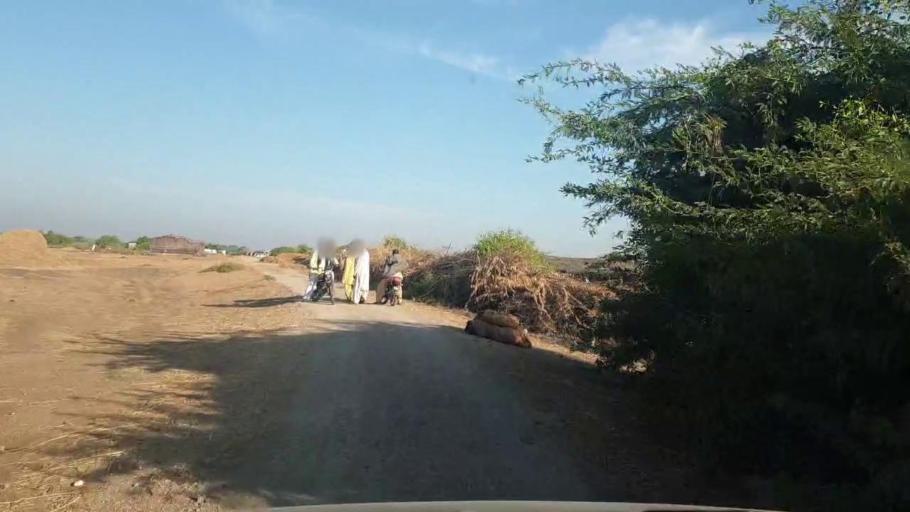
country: PK
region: Sindh
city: Talhar
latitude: 24.8266
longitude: 68.8407
